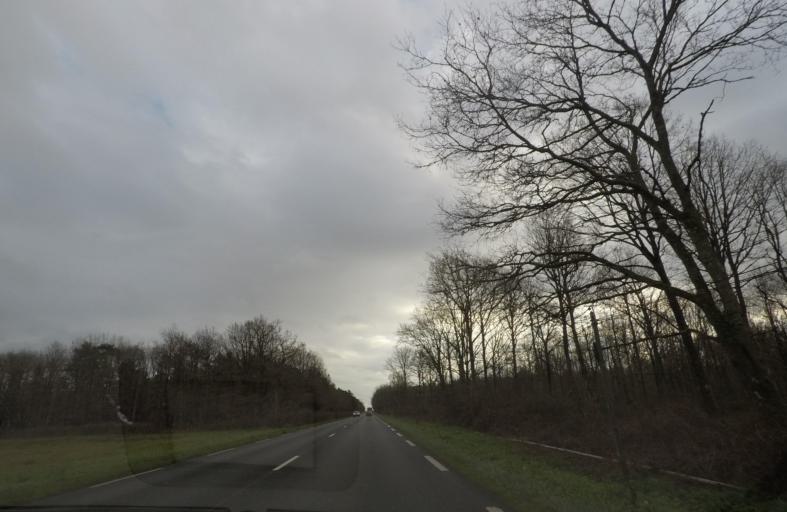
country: FR
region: Centre
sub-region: Departement du Loir-et-Cher
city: Mur-de-Sologne
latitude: 47.4214
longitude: 1.5866
